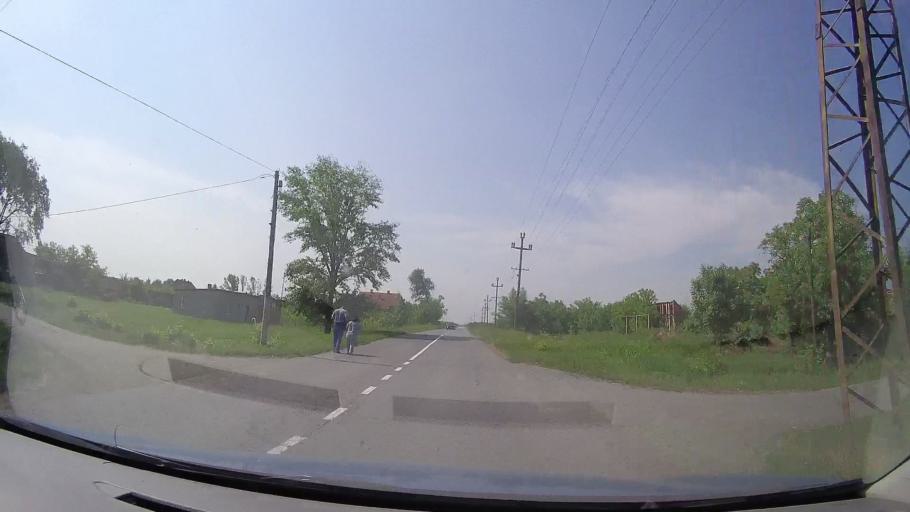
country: RS
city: Jarkovac
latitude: 45.2664
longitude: 20.7642
